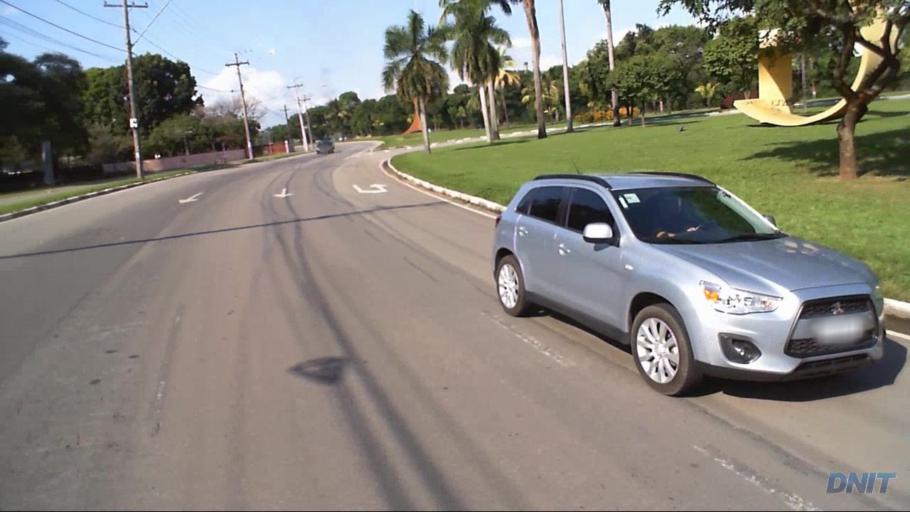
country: BR
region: Minas Gerais
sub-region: Ipatinga
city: Ipatinga
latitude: -19.4864
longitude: -42.5579
